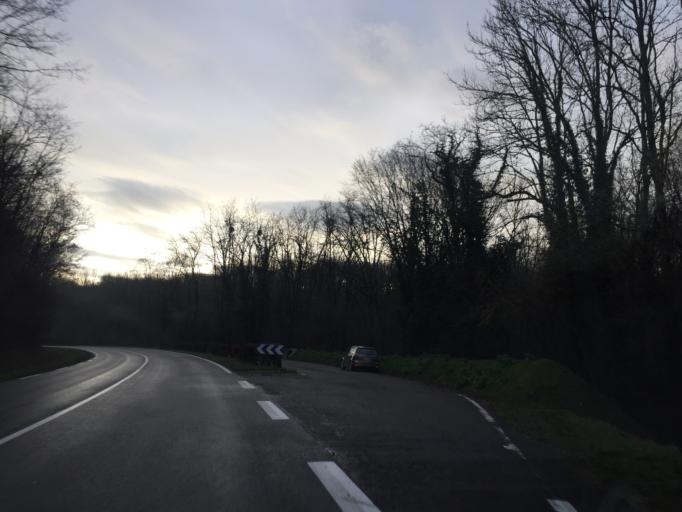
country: FR
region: Franche-Comte
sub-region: Departement du Jura
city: Choisey
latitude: 47.0041
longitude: 5.5045
